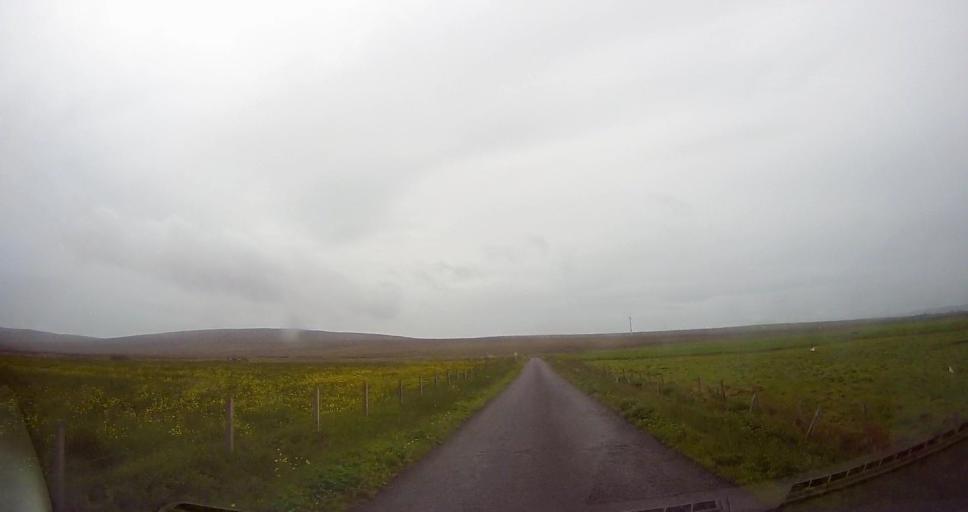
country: GB
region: Scotland
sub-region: Orkney Islands
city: Stromness
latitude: 59.0902
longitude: -3.1828
